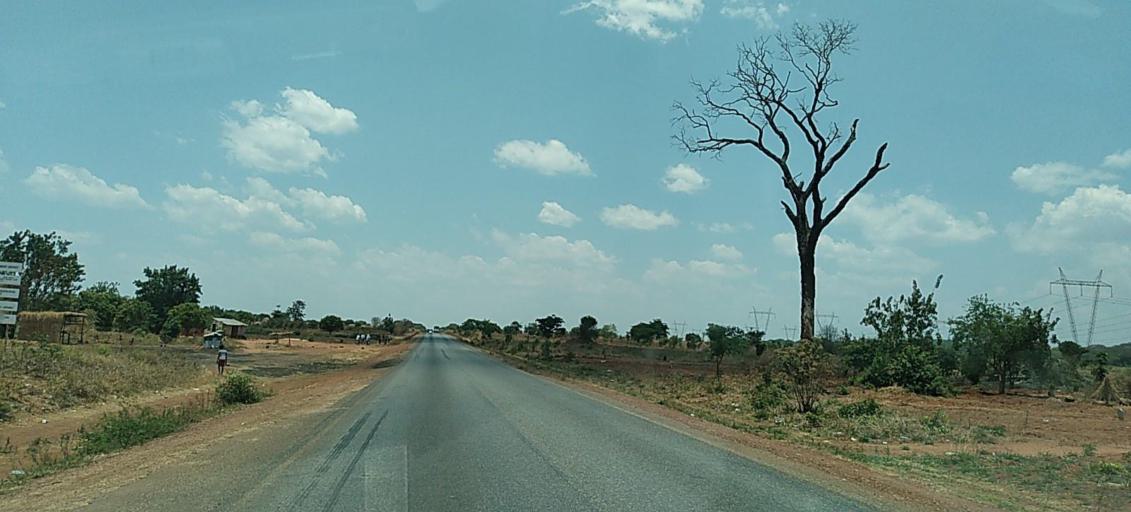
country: ZM
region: Central
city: Kapiri Mposhi
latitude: -13.7025
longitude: 28.6294
